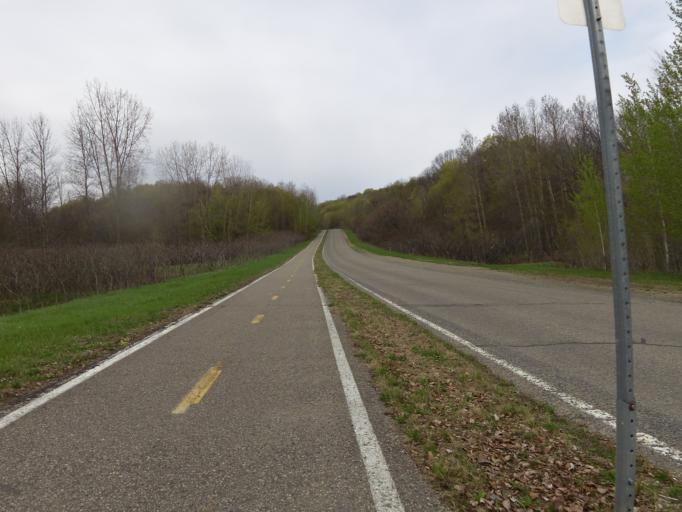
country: CA
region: Quebec
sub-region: Laurentides
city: Oka
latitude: 45.4824
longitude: -74.0349
